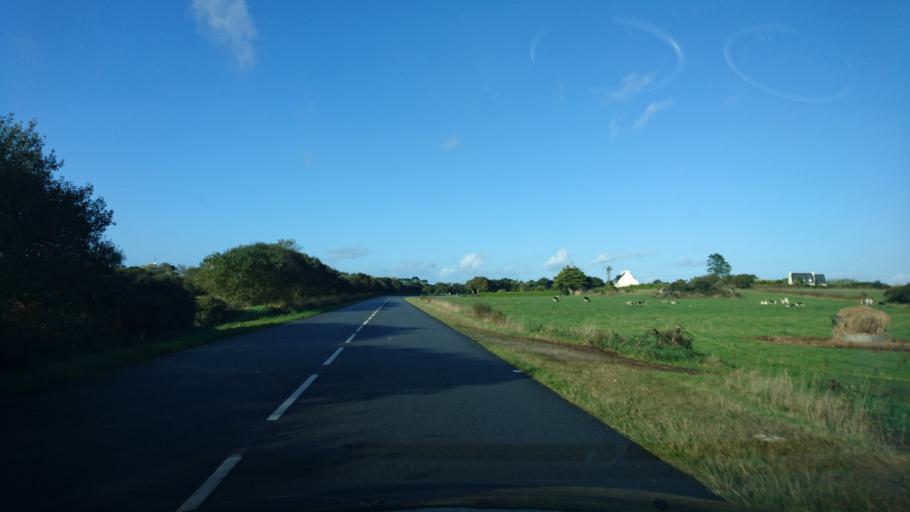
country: FR
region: Brittany
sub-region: Departement du Finistere
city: Plouarzel
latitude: 48.4383
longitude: -4.7275
